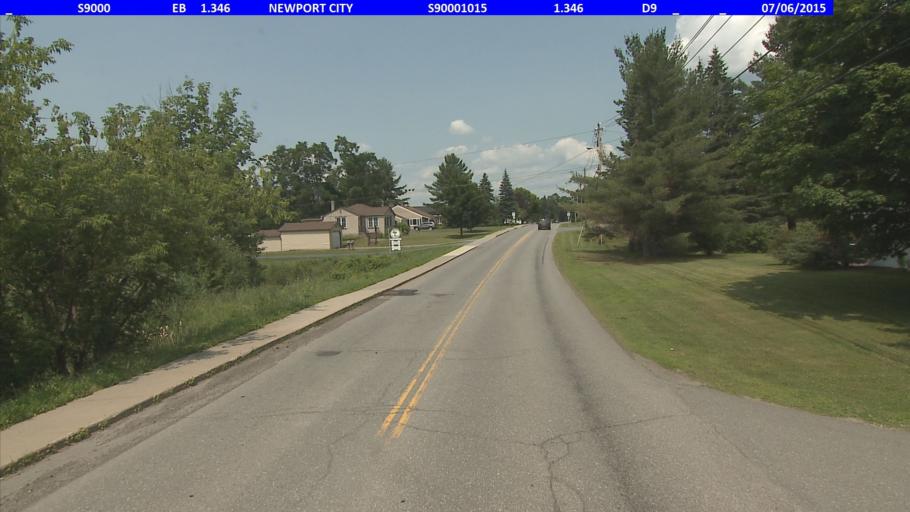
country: US
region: Vermont
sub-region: Orleans County
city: Newport
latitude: 44.9506
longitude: -72.1918
